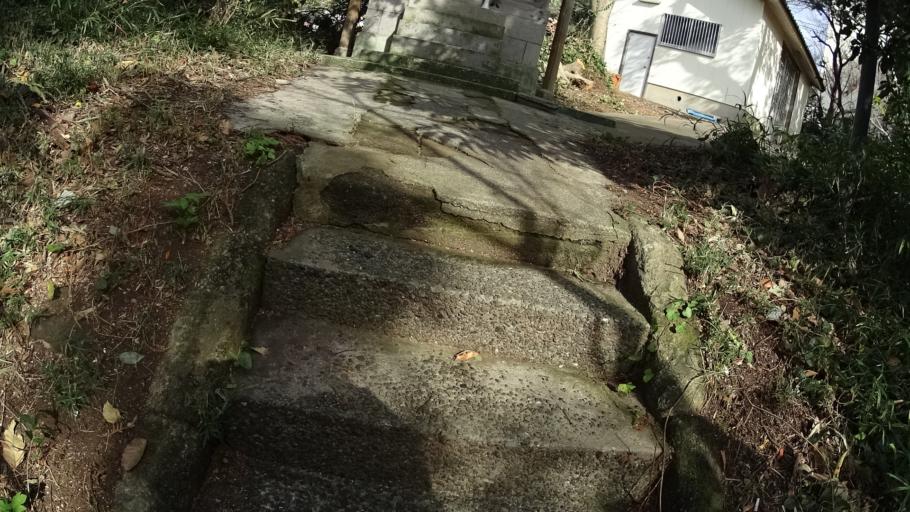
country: JP
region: Kanagawa
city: Miura
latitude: 35.1429
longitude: 139.6188
